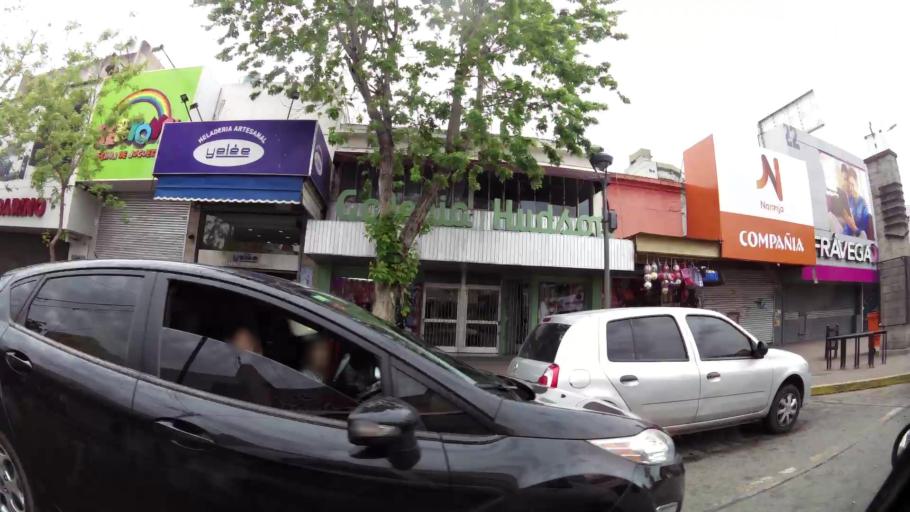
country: AR
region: Buenos Aires
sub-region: Partido de Quilmes
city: Quilmes
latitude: -34.7618
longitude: -58.2092
